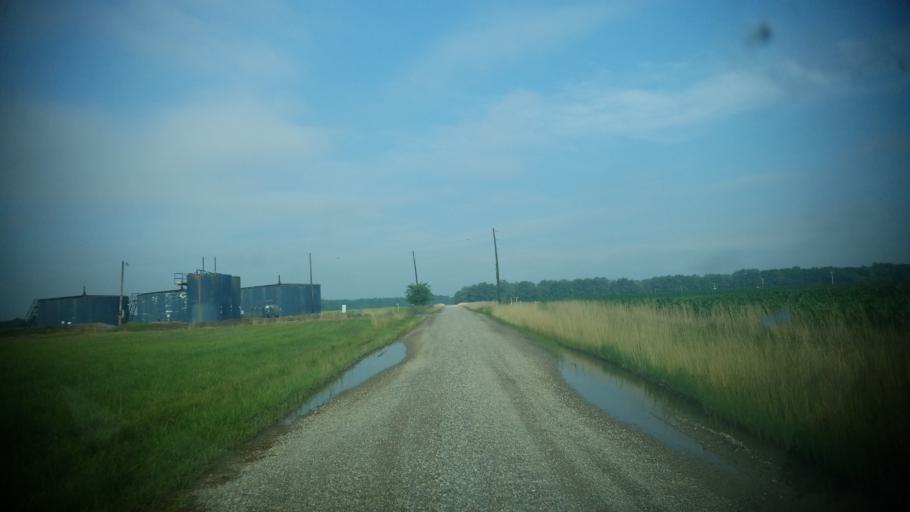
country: US
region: Illinois
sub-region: Clay County
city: Flora
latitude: 38.6017
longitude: -88.3495
